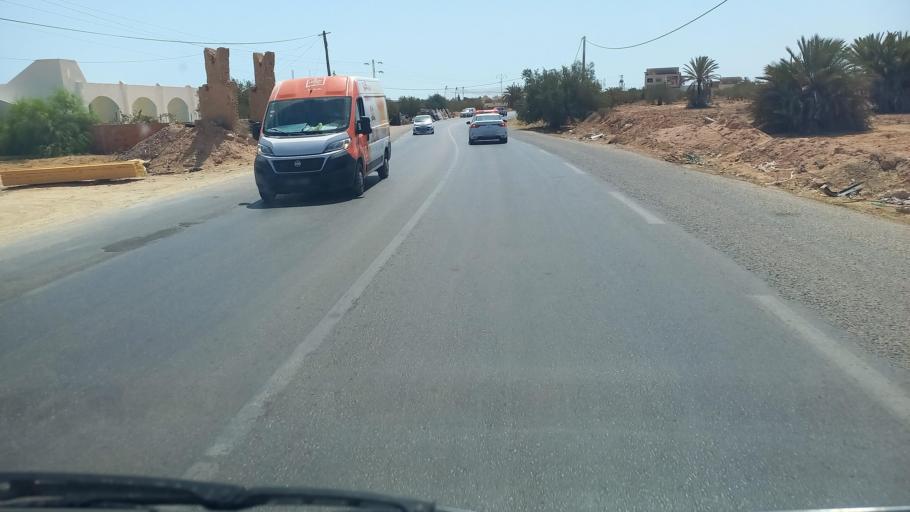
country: TN
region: Madanin
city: Houmt Souk
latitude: 33.8159
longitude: 10.8743
